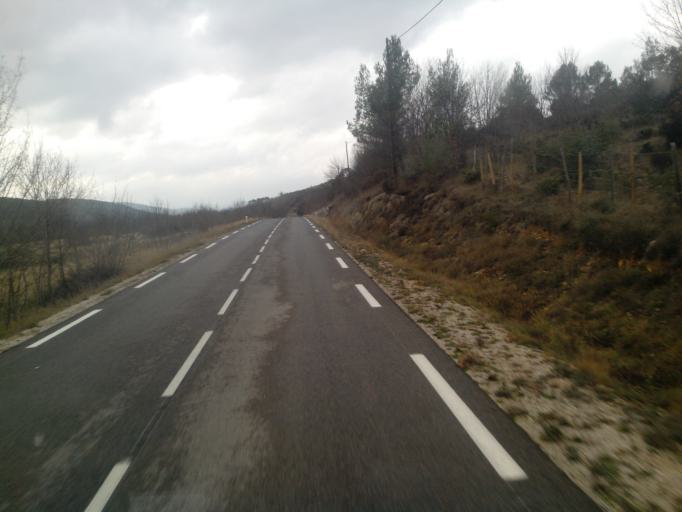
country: FR
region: Languedoc-Roussillon
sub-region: Departement de l'Herault
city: Saint-Bauzille-de-Putois
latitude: 43.9107
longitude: 3.7711
